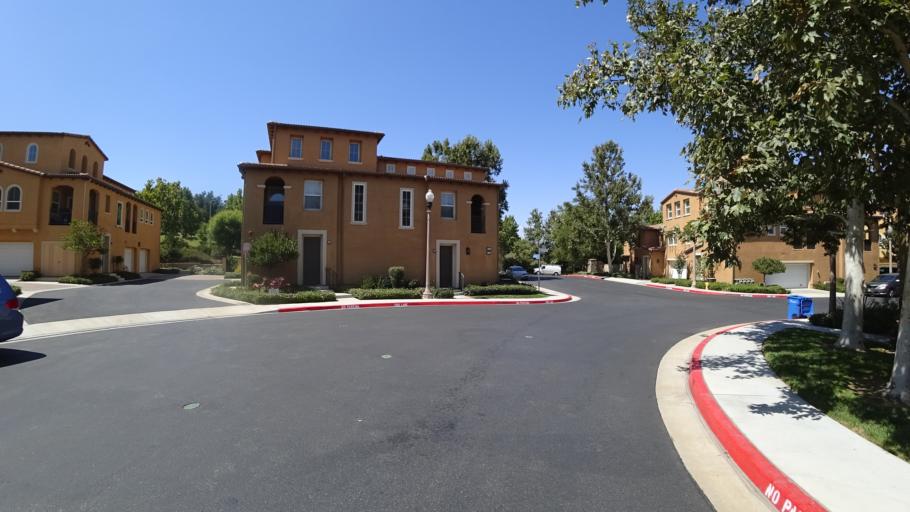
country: US
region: California
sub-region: Los Angeles County
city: Valencia
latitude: 34.4124
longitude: -118.5827
